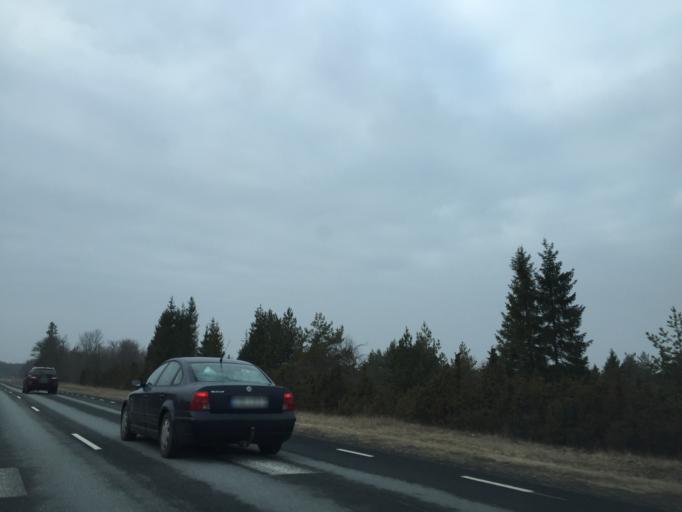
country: EE
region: Saare
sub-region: Orissaare vald
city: Orissaare
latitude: 58.5895
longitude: 23.3383
